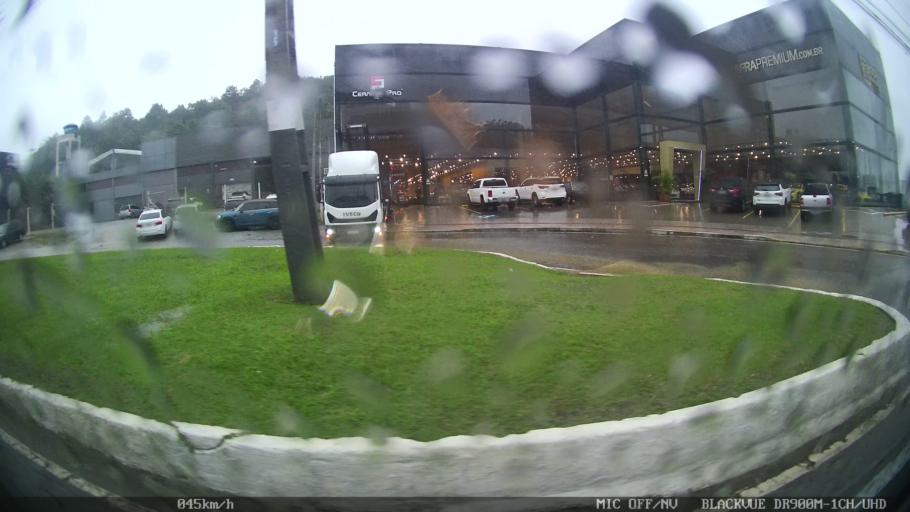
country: BR
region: Santa Catarina
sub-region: Balneario Camboriu
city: Balneario Camboriu
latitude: -26.9600
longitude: -48.6399
